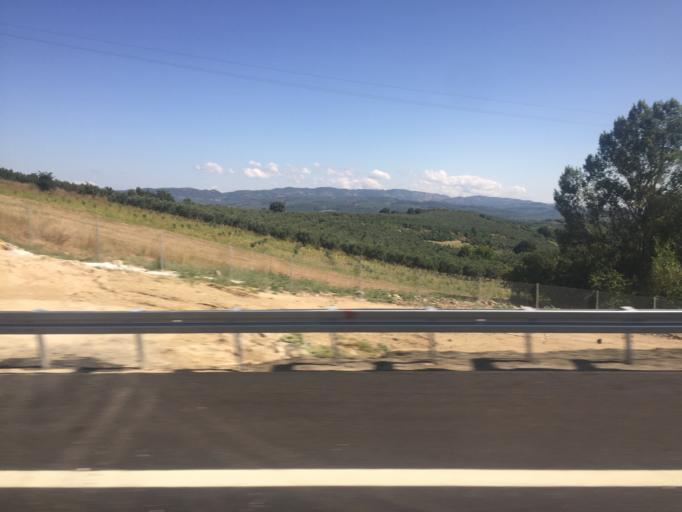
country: TR
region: Bursa
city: Gorukle
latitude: 40.2540
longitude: 28.7417
